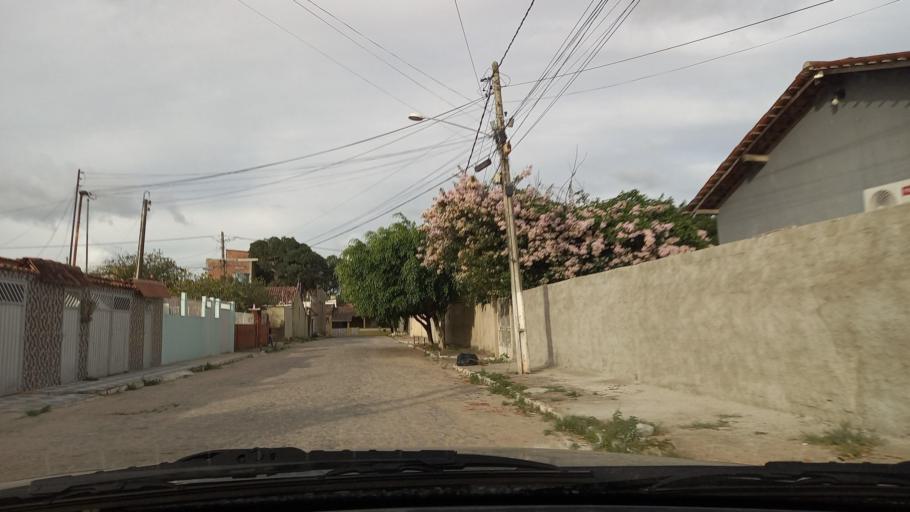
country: BR
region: Pernambuco
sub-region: Gravata
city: Gravata
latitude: -8.2000
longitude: -35.5598
